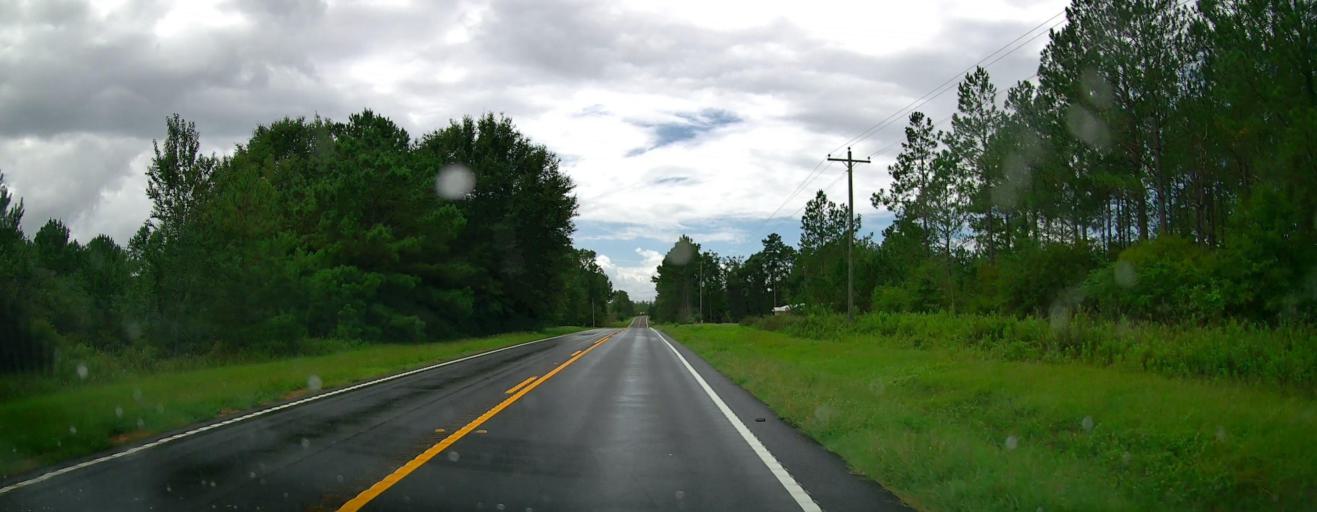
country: US
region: Georgia
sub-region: Pulaski County
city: Hawkinsville
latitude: 32.1713
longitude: -83.5399
